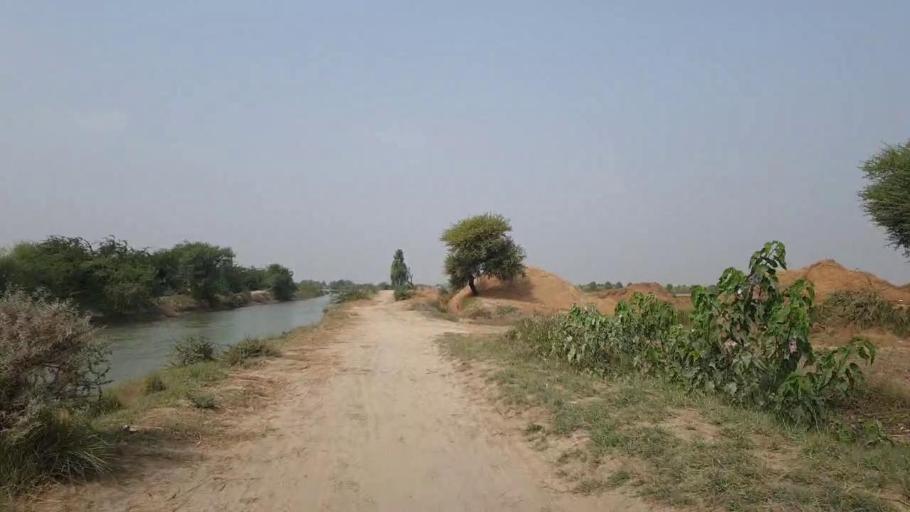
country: PK
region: Sindh
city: Kario
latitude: 24.8480
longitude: 68.5331
